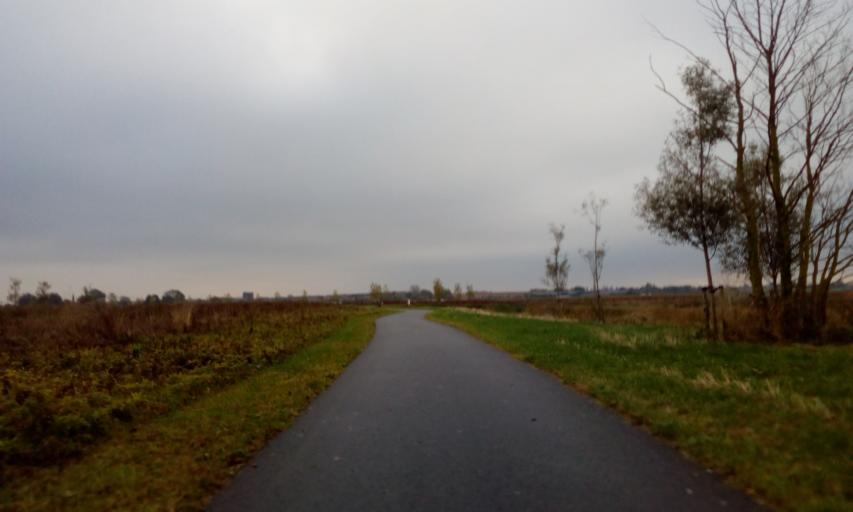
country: NL
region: South Holland
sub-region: Gemeente Lansingerland
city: Berkel en Rodenrijs
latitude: 52.0090
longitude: 4.4661
